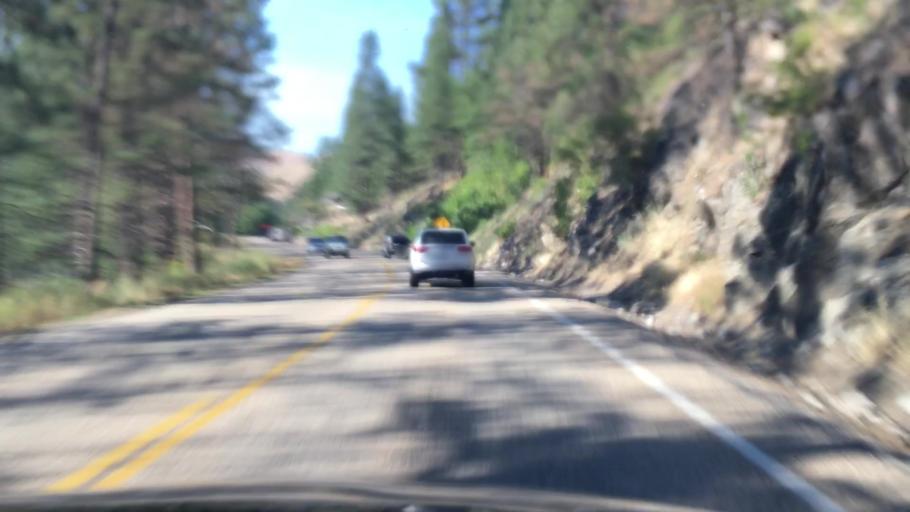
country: US
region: Idaho
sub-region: Boise County
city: Idaho City
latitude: 44.0649
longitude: -116.1210
